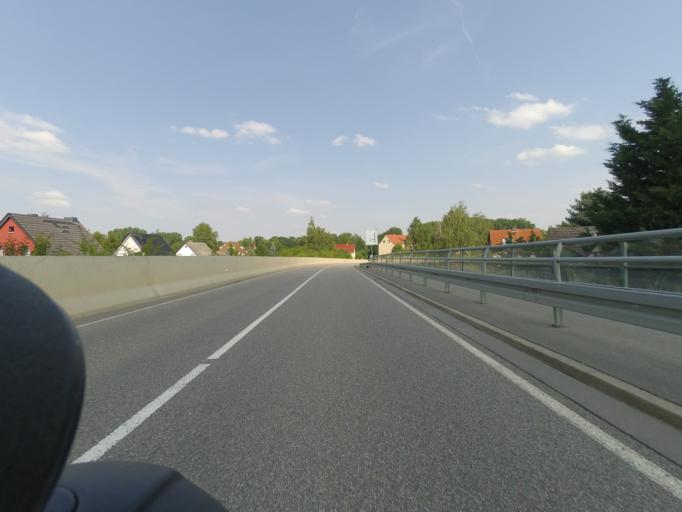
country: DE
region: Thuringia
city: Gerstenberg
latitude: 51.0325
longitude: 12.4366
